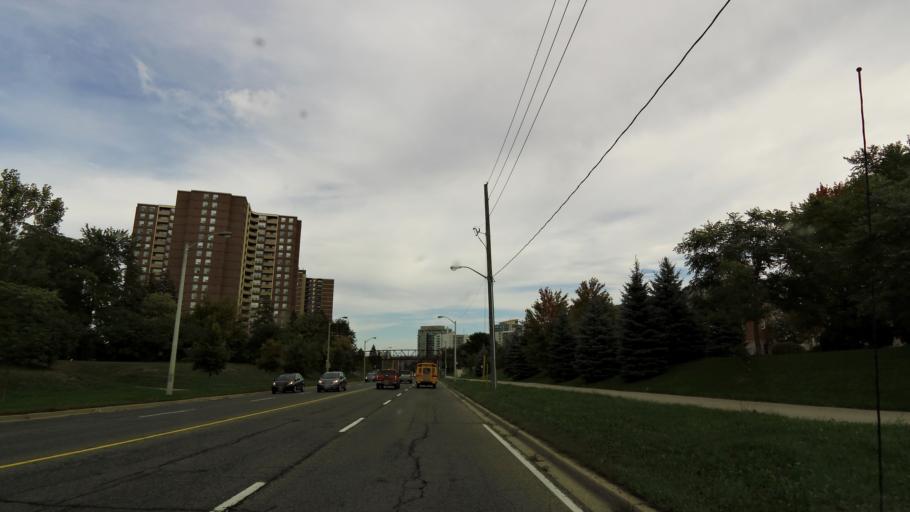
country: CA
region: Ontario
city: Etobicoke
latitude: 43.6834
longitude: -79.5187
